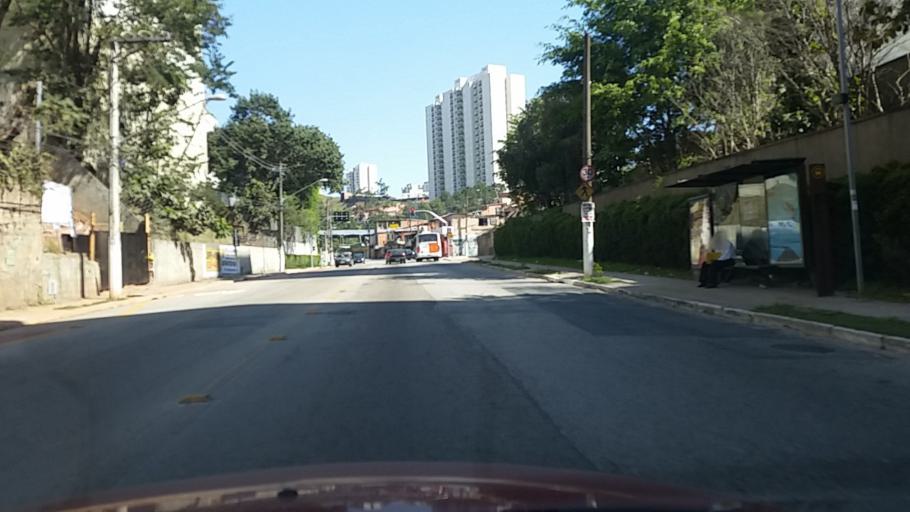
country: BR
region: Sao Paulo
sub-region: Taboao Da Serra
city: Taboao da Serra
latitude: -23.6168
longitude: -46.7428
